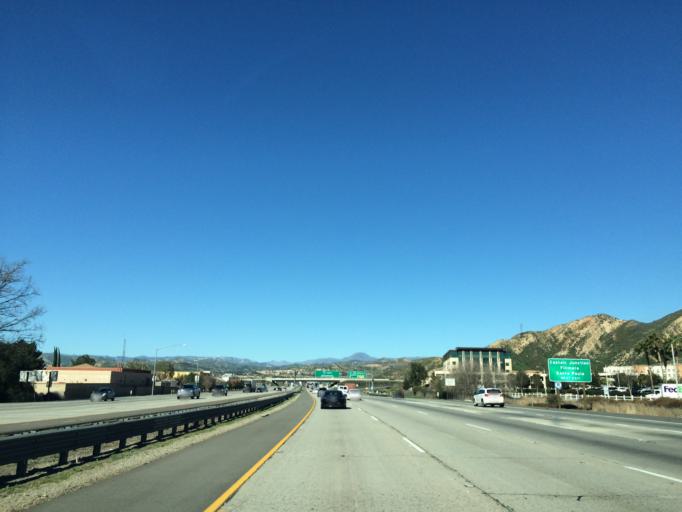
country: US
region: California
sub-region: Los Angeles County
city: Valencia
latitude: 34.4394
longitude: -118.5980
